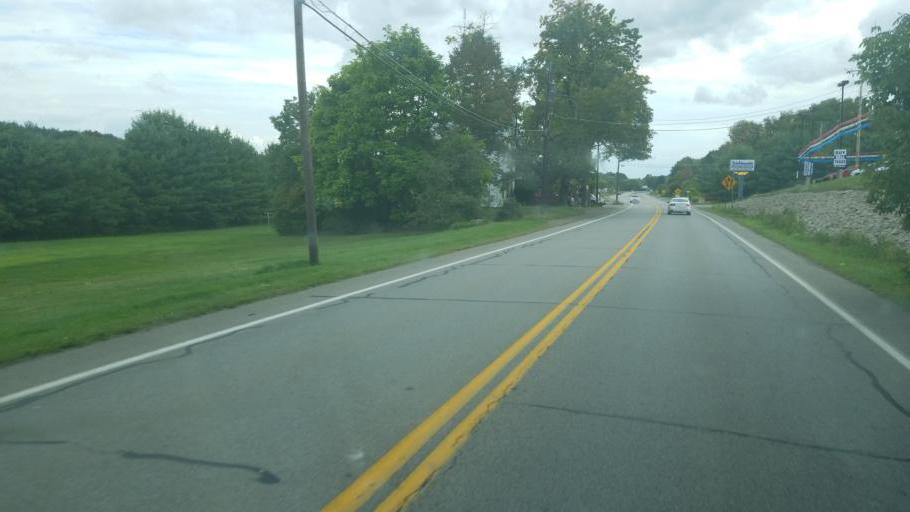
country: US
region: Pennsylvania
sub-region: Mercer County
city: Greenville
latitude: 41.3836
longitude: -80.3962
